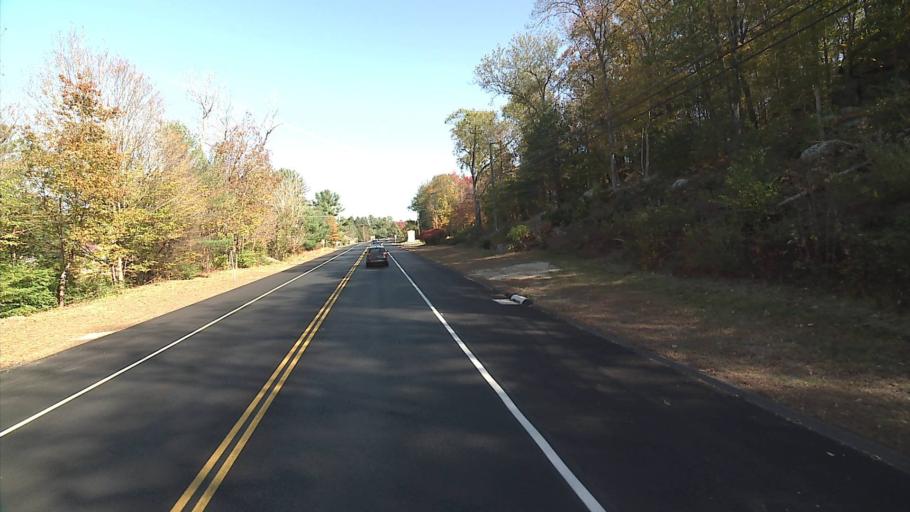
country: US
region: Connecticut
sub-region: Windham County
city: Windham
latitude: 41.7540
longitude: -72.1499
